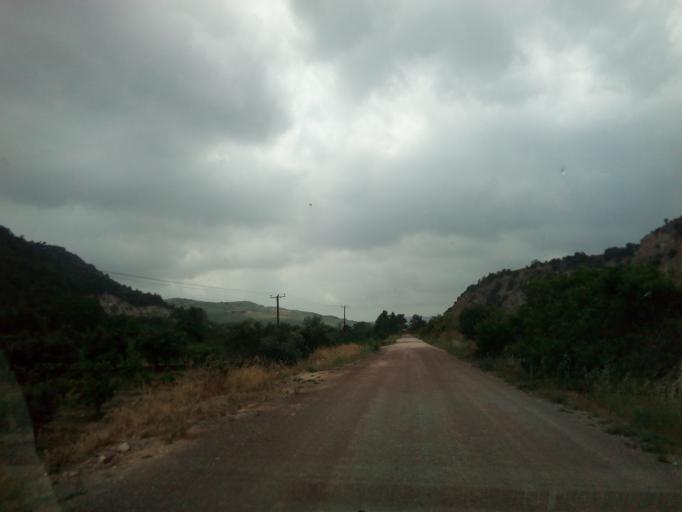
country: CY
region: Pafos
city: Mesogi
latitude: 34.8080
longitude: 32.6138
